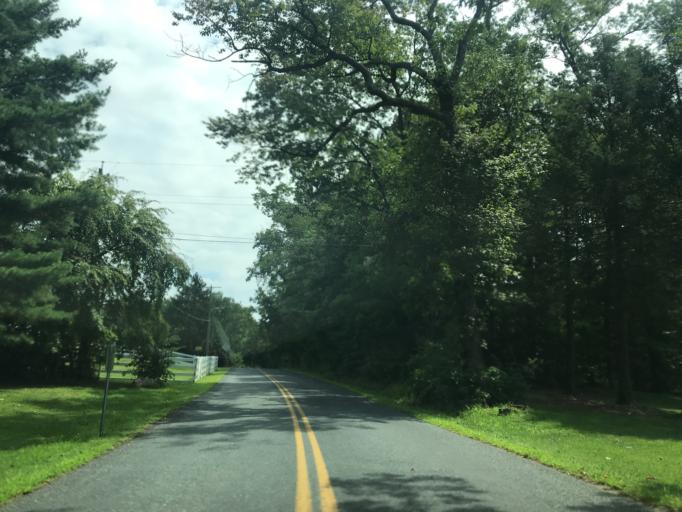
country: US
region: Maryland
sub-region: Harford County
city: Pleasant Hills
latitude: 39.4884
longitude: -76.4173
